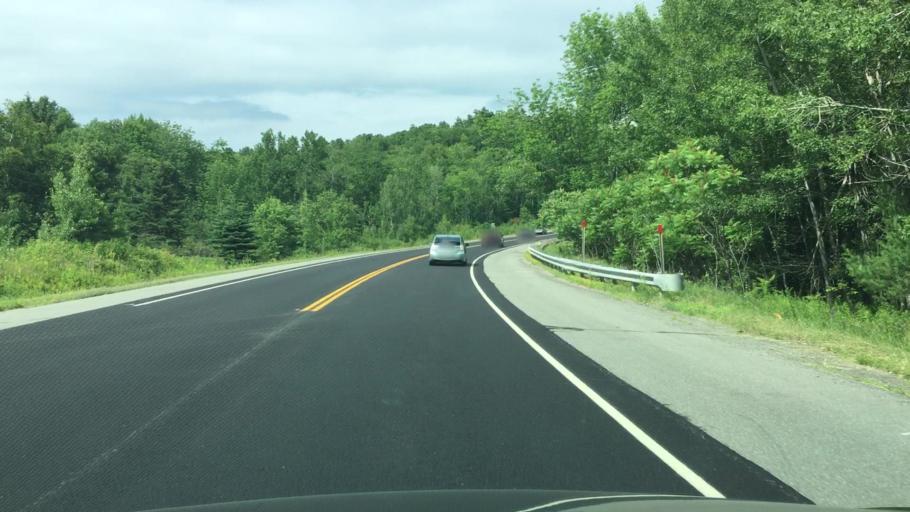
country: US
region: Maine
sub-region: Hancock County
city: Bucksport
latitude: 44.5544
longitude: -68.8101
